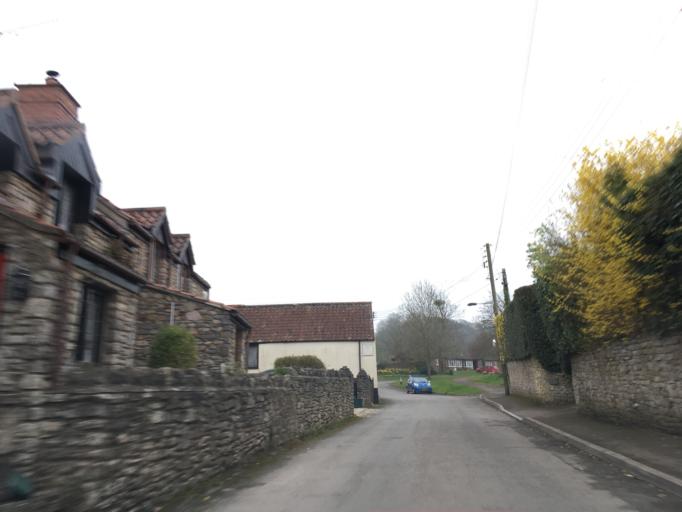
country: GB
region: England
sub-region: South Gloucestershire
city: Almondsbury
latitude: 51.5828
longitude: -2.5755
